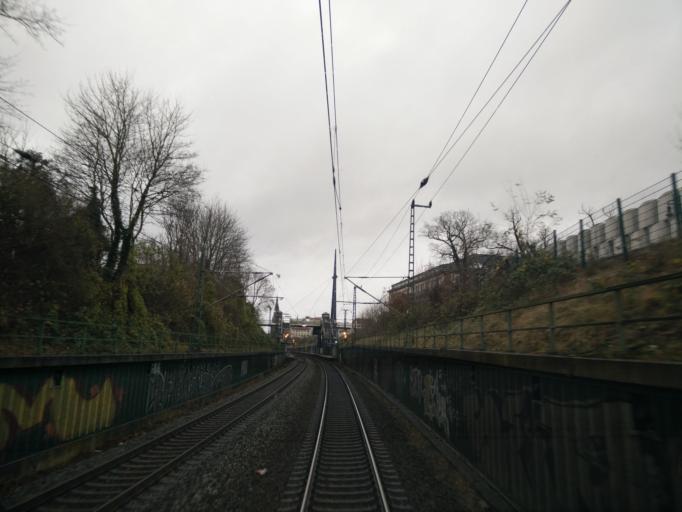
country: DE
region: Mecklenburg-Vorpommern
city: Feldstadt
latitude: 53.6253
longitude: 11.4044
